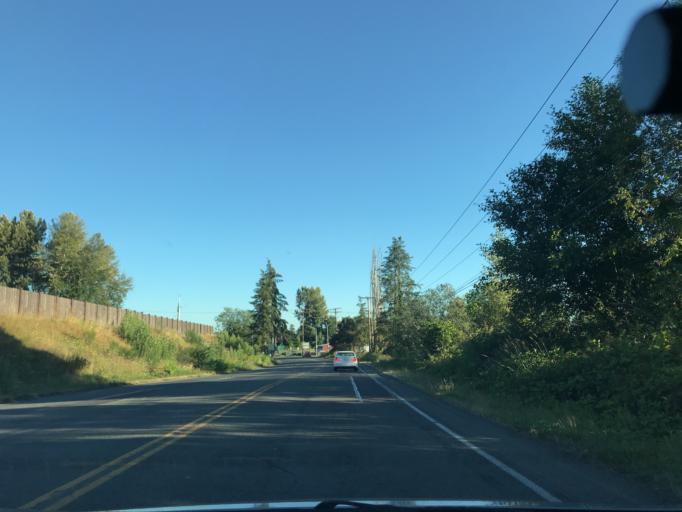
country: US
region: Washington
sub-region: Pierce County
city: Bonney Lake
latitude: 47.2008
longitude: -122.2081
